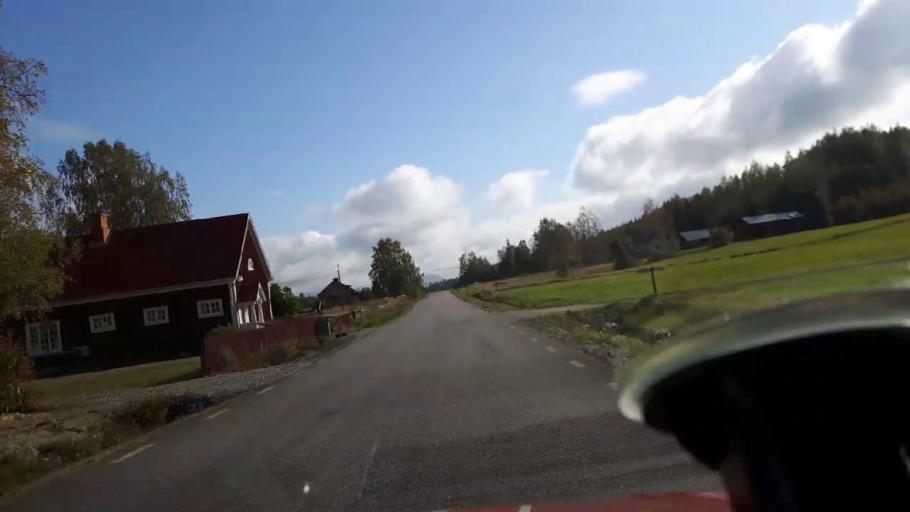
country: SE
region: Gaevleborg
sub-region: Ljusdals Kommun
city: Ljusdal
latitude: 61.7658
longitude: 16.0459
